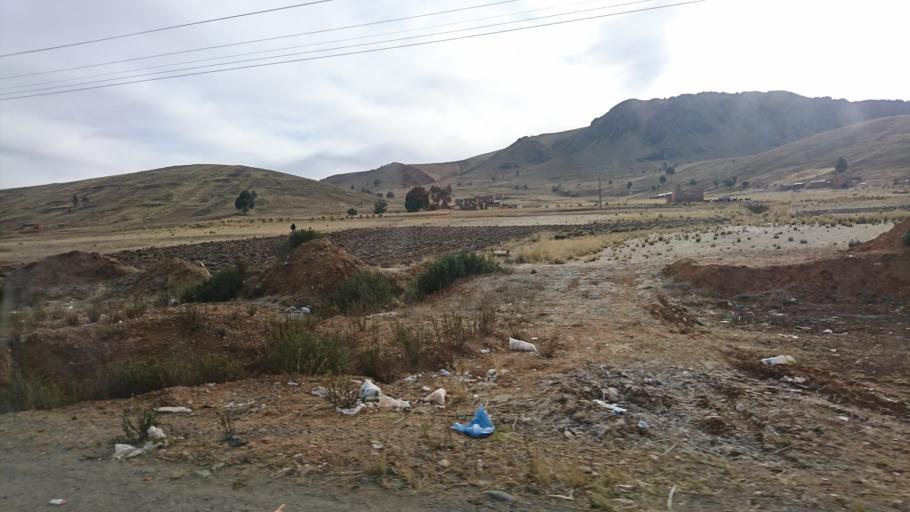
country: BO
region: La Paz
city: La Paz
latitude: -16.4138
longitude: -68.3458
